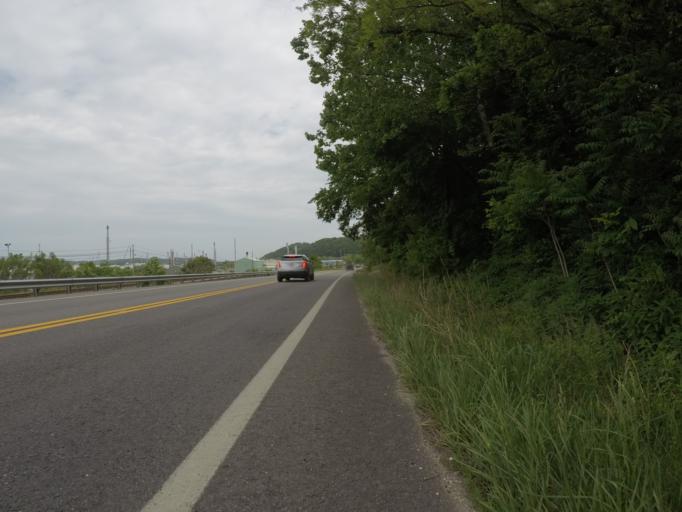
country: US
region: West Virginia
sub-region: Wayne County
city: Kenova
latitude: 38.3685
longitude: -82.5921
